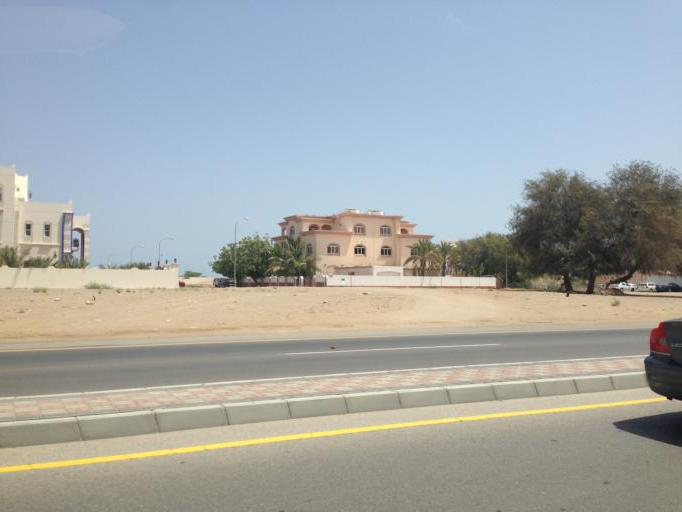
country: OM
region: Muhafazat Masqat
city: Bawshar
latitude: 23.6023
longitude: 58.3591
